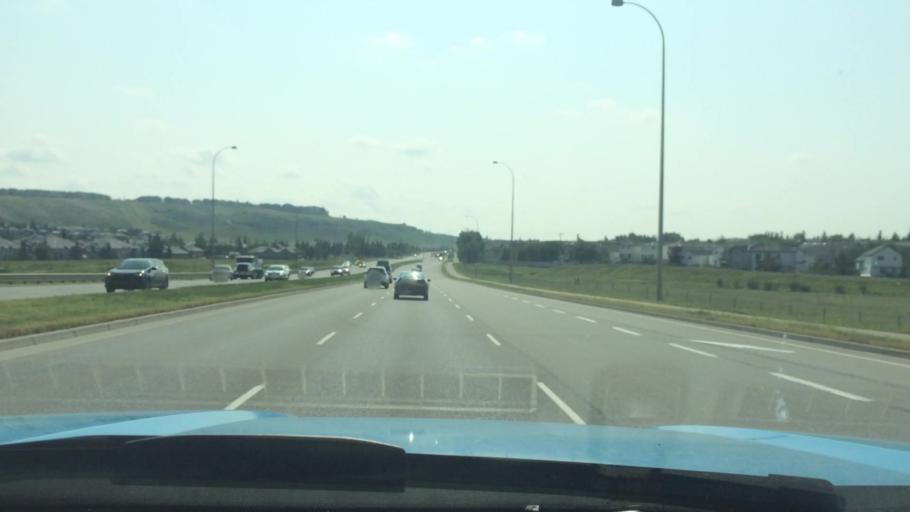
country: CA
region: Alberta
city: Calgary
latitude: 51.1556
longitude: -114.1125
